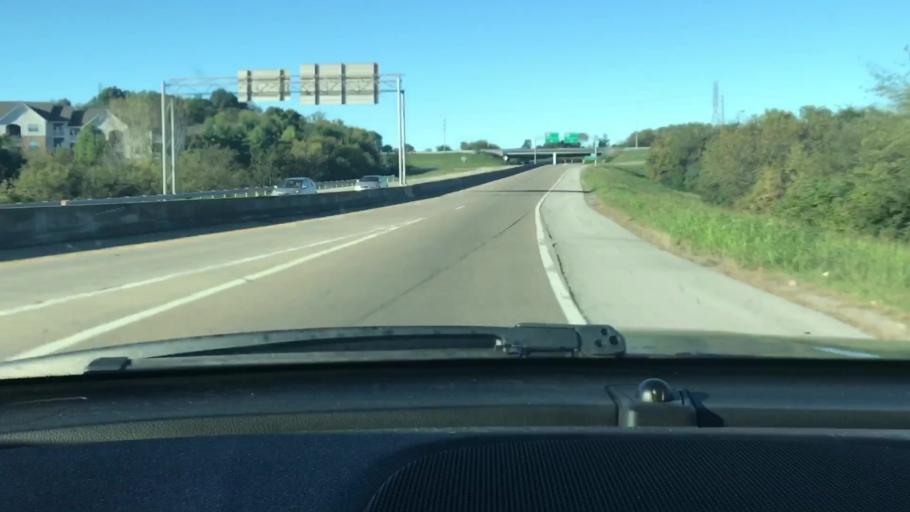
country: US
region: Tennessee
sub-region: Sumner County
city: Hendersonville
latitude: 36.3097
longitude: -86.6569
